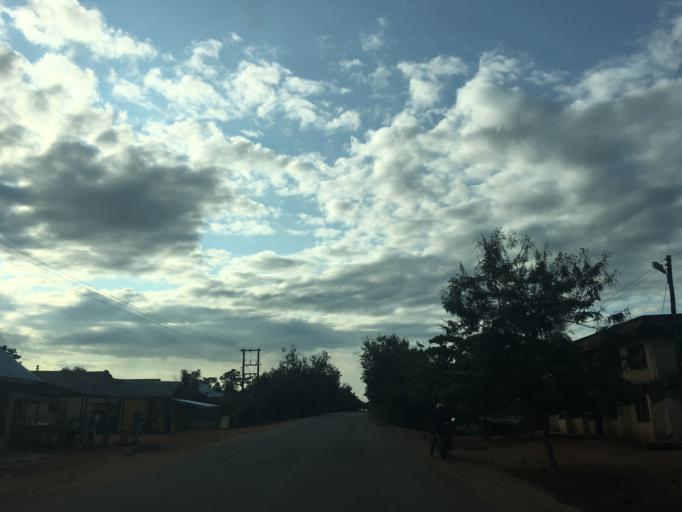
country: GH
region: Western
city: Bibiani
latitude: 6.3391
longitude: -2.2719
